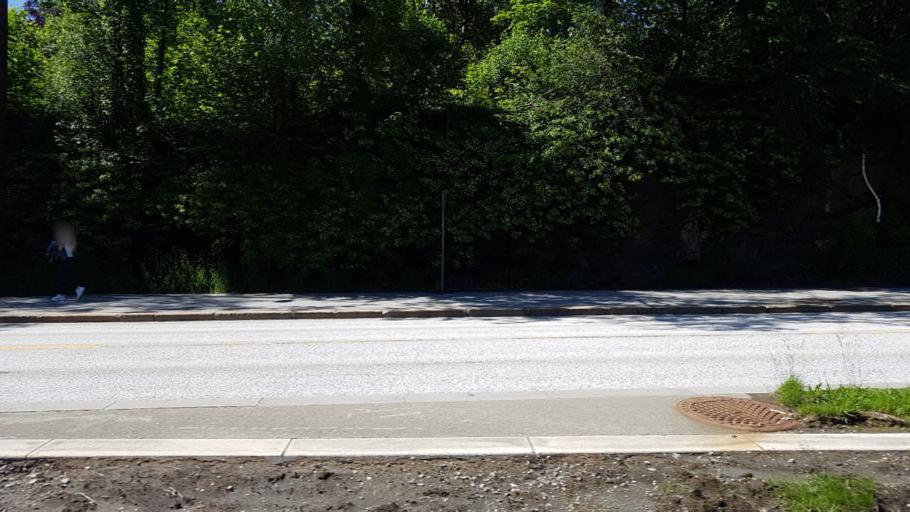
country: NO
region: Hordaland
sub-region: Bergen
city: Bergen
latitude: 60.3346
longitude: 5.3442
